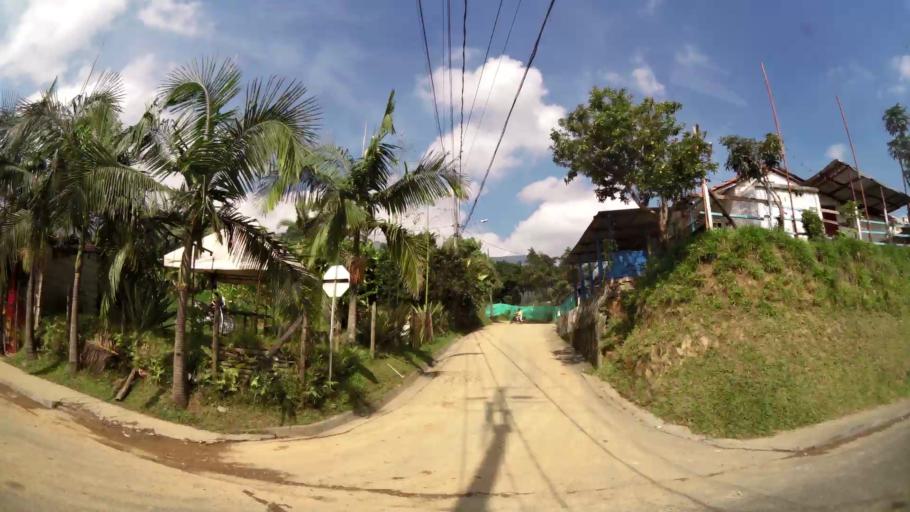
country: CO
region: Antioquia
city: La Estrella
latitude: 6.1704
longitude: -75.6494
